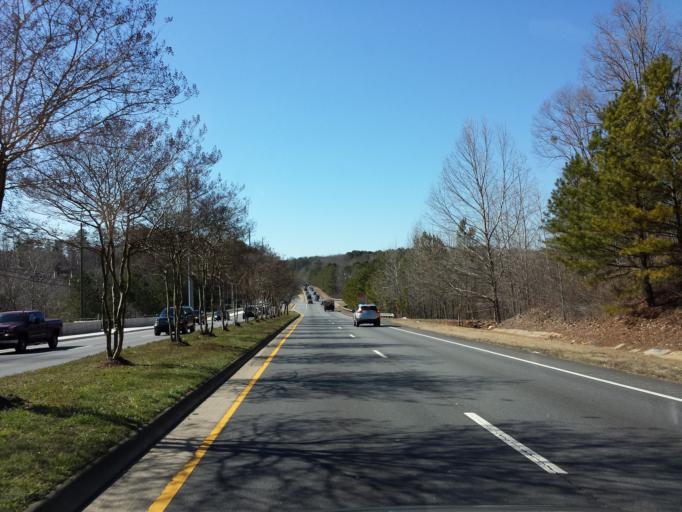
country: US
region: Georgia
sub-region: Cobb County
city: Kennesaw
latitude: 33.9482
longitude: -84.6342
